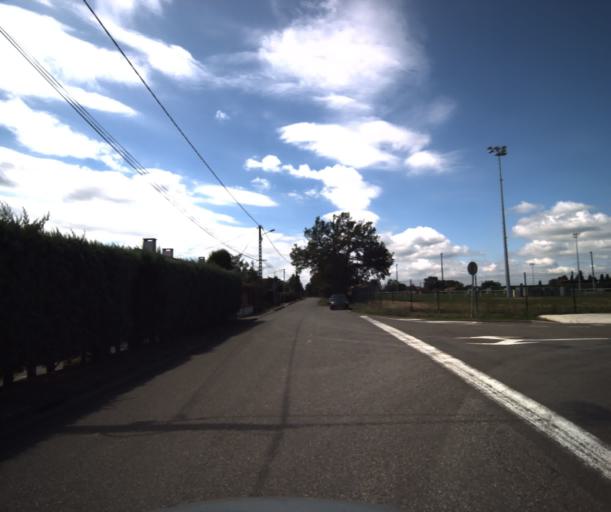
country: FR
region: Midi-Pyrenees
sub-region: Departement de la Haute-Garonne
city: Lacasse
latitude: 43.3945
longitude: 1.2663
